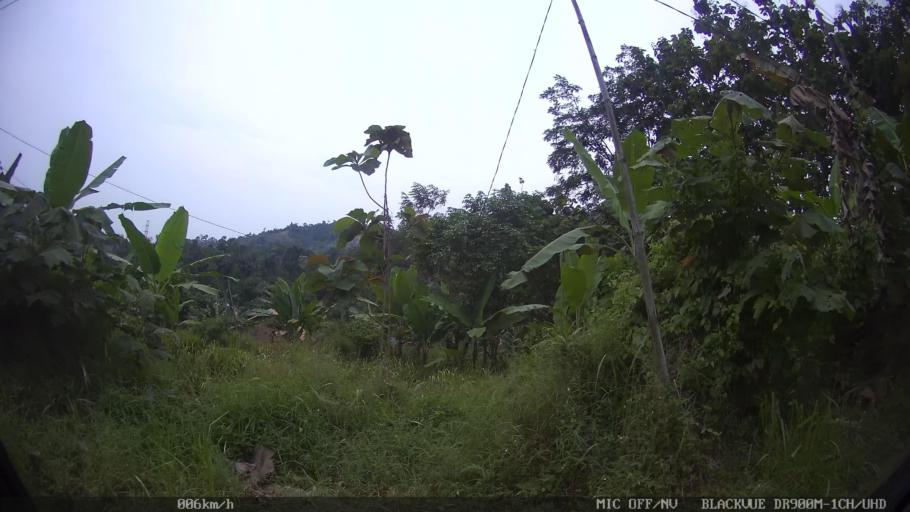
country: ID
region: Lampung
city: Panjang
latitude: -5.4281
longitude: 105.3395
